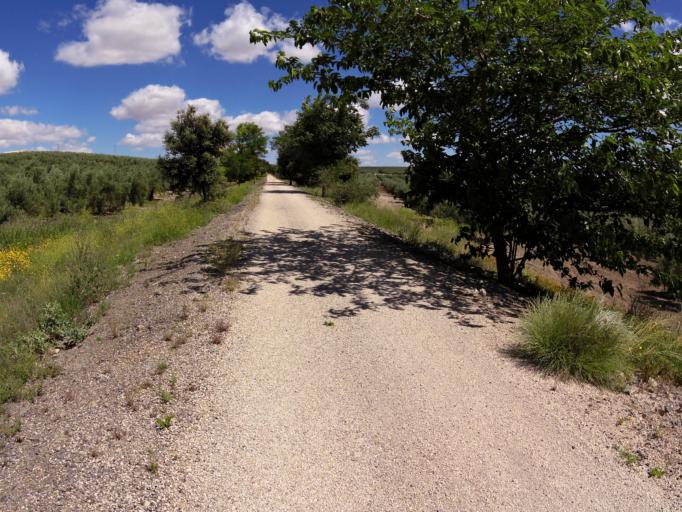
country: ES
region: Andalusia
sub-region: Provincia de Jaen
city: Alcaudete
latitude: 37.6553
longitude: -4.0620
